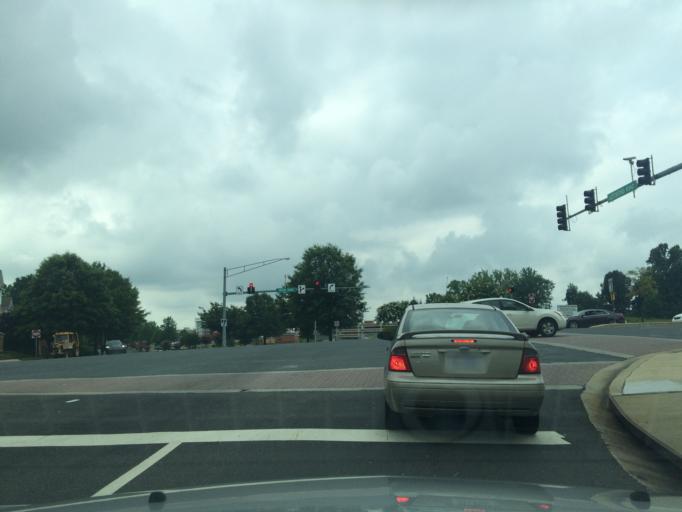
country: US
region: Maryland
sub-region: Prince George's County
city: Lake Arbor
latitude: 38.9042
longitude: -76.8417
